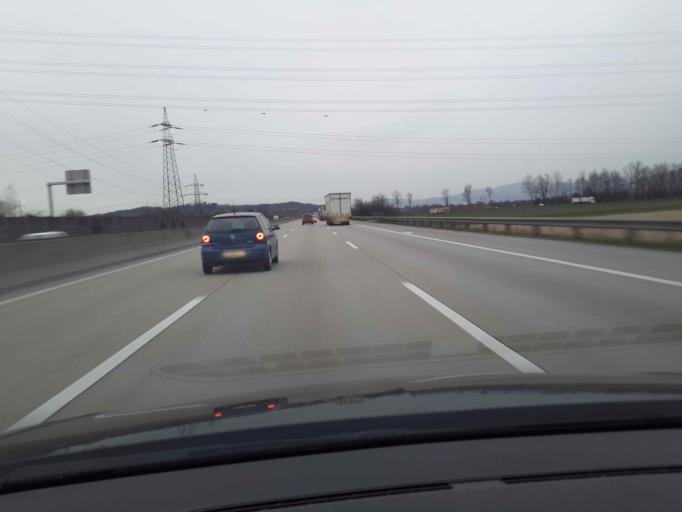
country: AT
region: Upper Austria
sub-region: Politischer Bezirk Linz-Land
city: Sankt Florian
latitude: 48.2268
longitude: 14.3890
